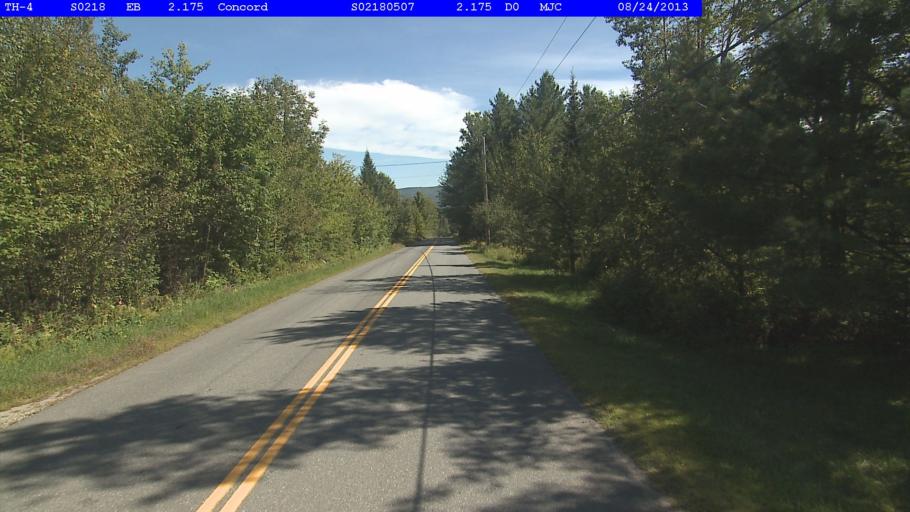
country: US
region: New Hampshire
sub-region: Grafton County
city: Littleton
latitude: 44.4364
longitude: -71.7583
